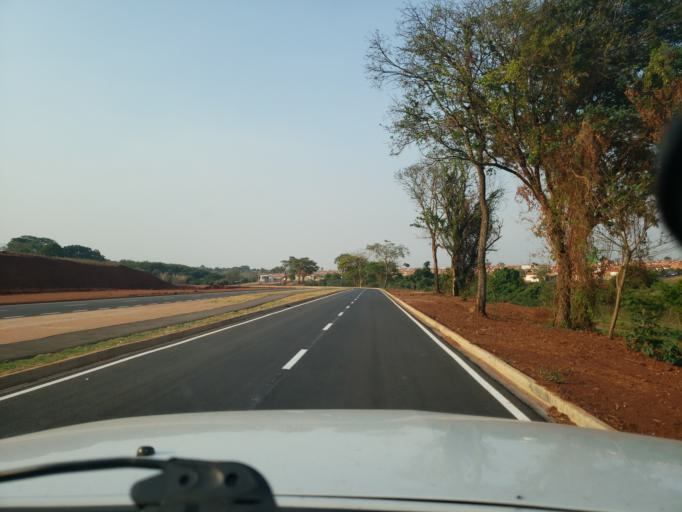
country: BR
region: Sao Paulo
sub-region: Moji-Guacu
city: Mogi-Gaucu
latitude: -22.3202
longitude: -46.9468
